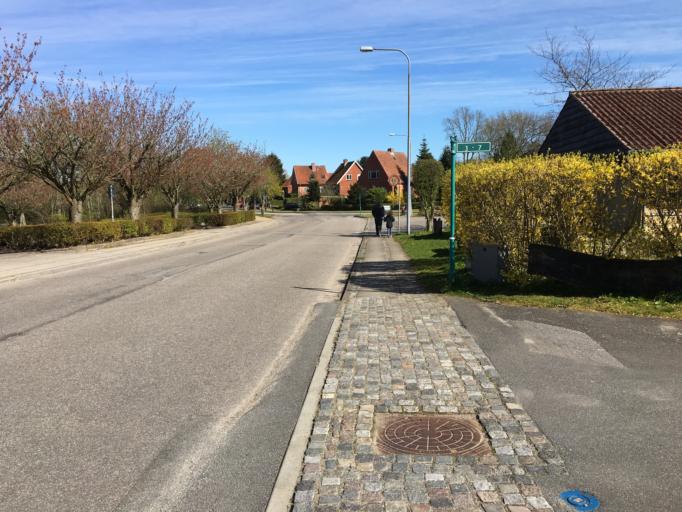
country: DK
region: South Denmark
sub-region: Middelfart Kommune
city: Middelfart
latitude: 55.5031
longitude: 9.7131
